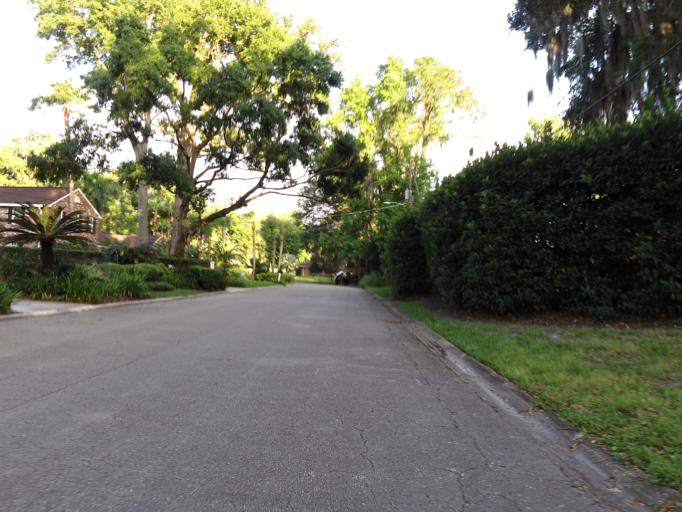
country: US
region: Florida
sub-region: Clay County
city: Orange Park
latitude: 30.2144
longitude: -81.6227
